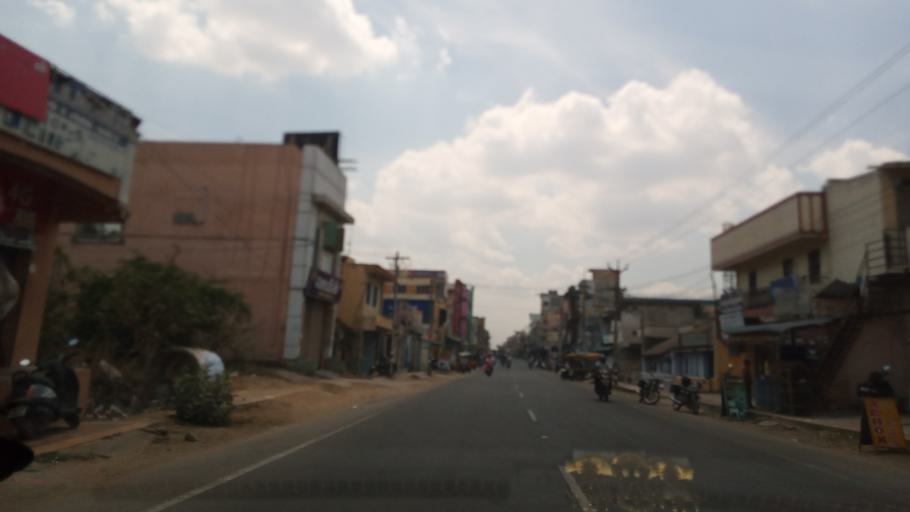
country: IN
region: Tamil Nadu
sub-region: Vellore
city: Walajapet
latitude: 12.9251
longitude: 79.3681
